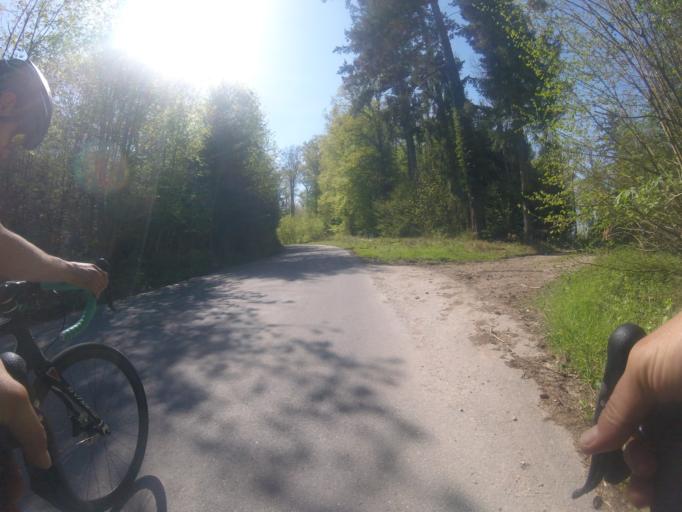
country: CH
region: Bern
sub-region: Bern-Mittelland District
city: Laupen
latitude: 46.9036
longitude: 7.2472
